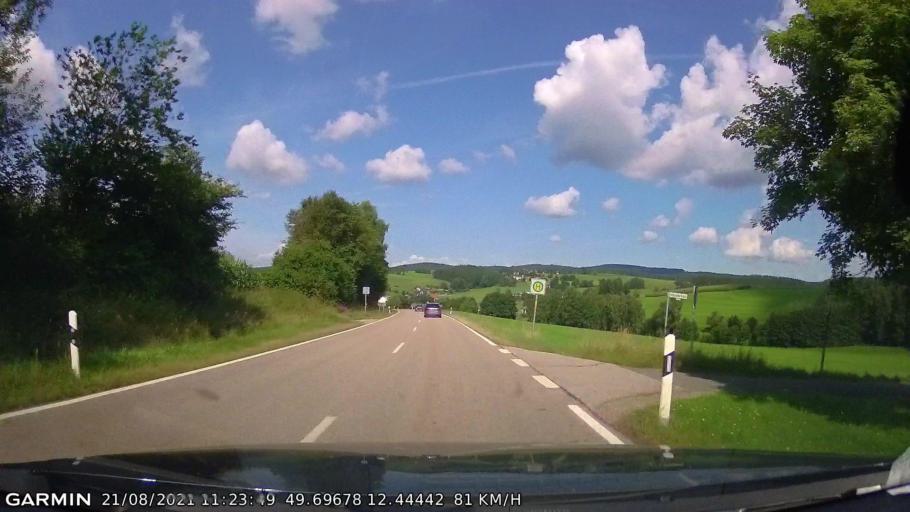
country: DE
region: Bavaria
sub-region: Upper Palatinate
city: Georgenberg
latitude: 49.6968
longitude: 12.4444
